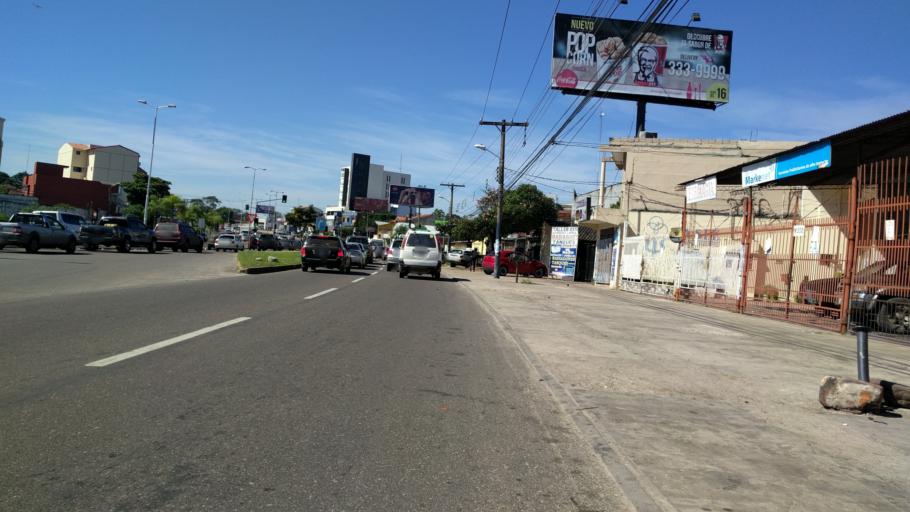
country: BO
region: Santa Cruz
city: Santa Cruz de la Sierra
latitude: -17.8006
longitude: -63.1905
